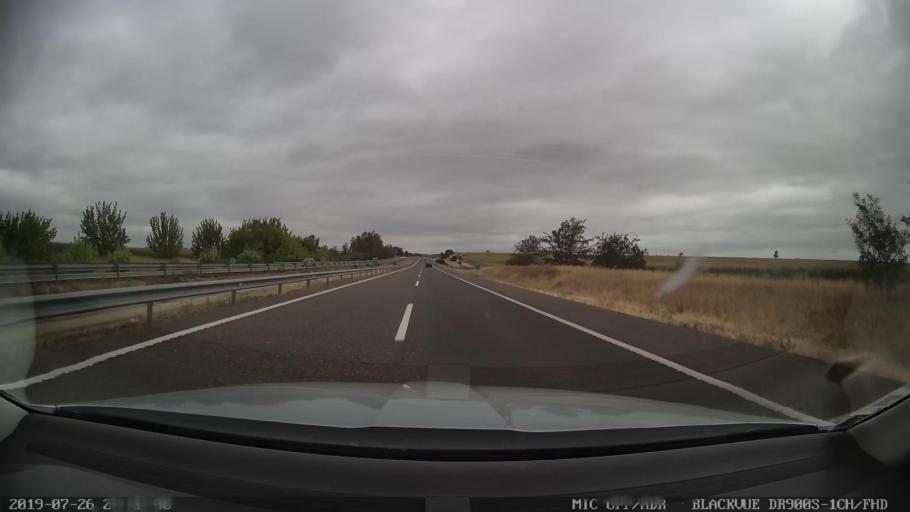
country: ES
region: Extremadura
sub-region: Provincia de Badajoz
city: Santa Amalia
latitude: 39.0133
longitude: -6.0867
